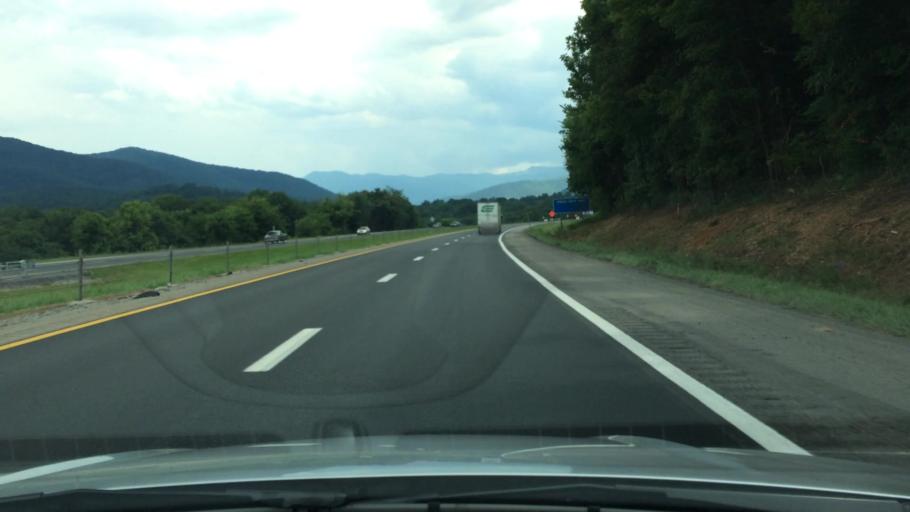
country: US
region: Tennessee
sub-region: Cocke County
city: Newport
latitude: 35.9008
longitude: -83.1840
